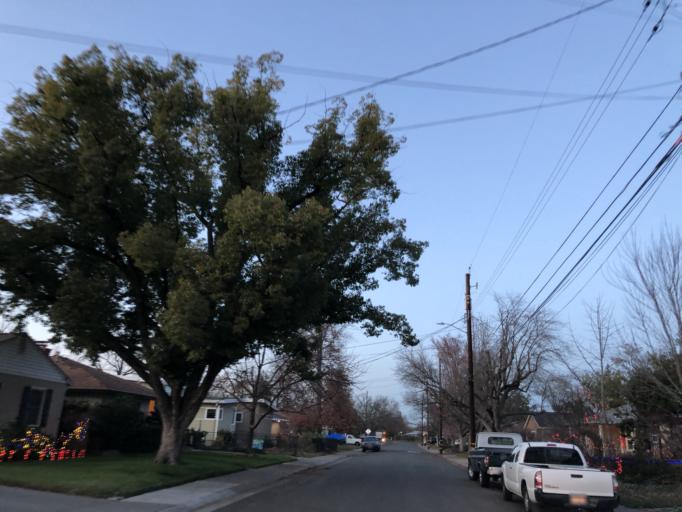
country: US
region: California
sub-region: Sacramento County
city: Parkway
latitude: 38.5486
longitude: -121.4380
